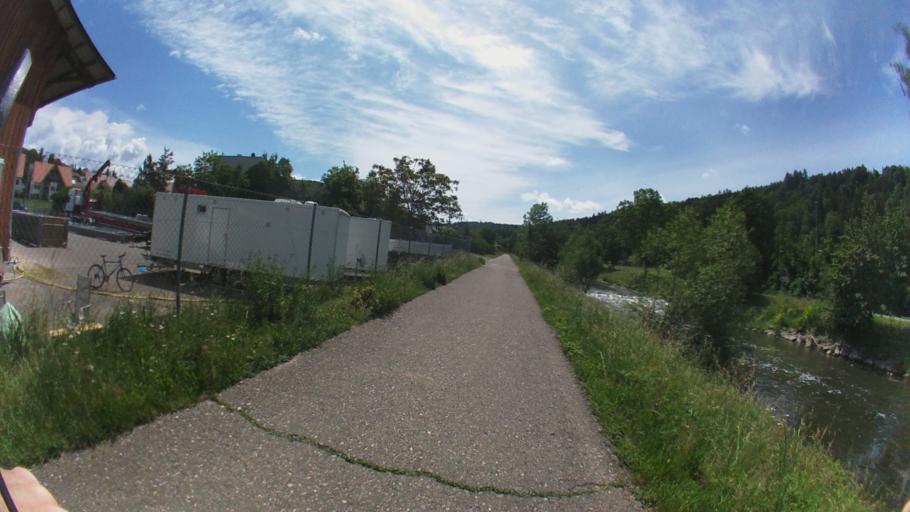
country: CH
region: Zurich
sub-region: Bezirk Buelach
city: Glattfelden
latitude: 47.5588
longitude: 8.4954
